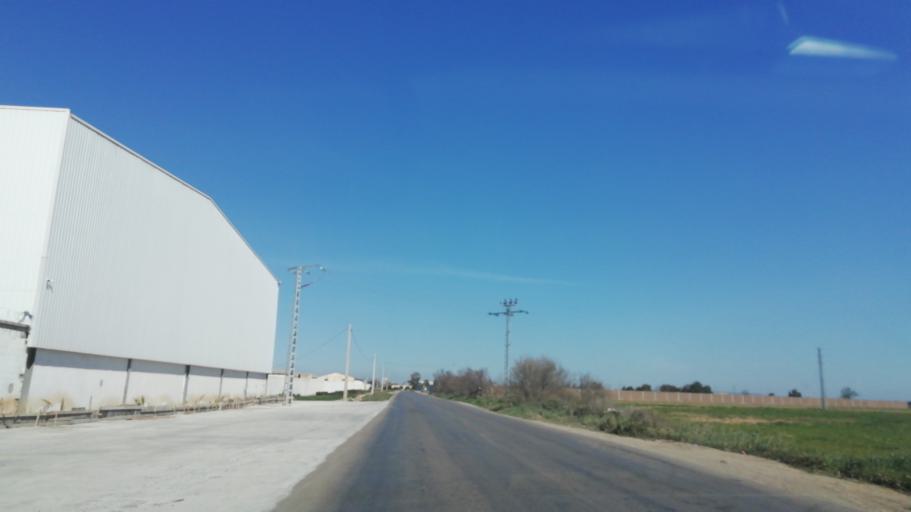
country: DZ
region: Oran
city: Es Senia
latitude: 35.5102
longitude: -0.5911
